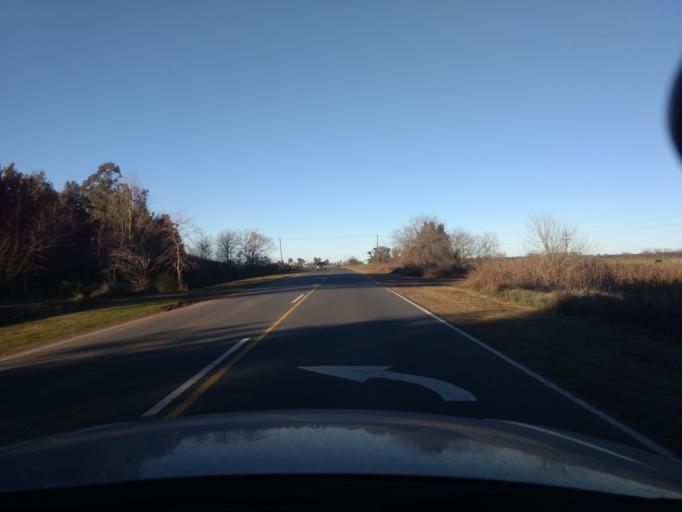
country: AR
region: Buenos Aires
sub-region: Partido de Lujan
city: Lujan
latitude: -34.6268
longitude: -59.1085
